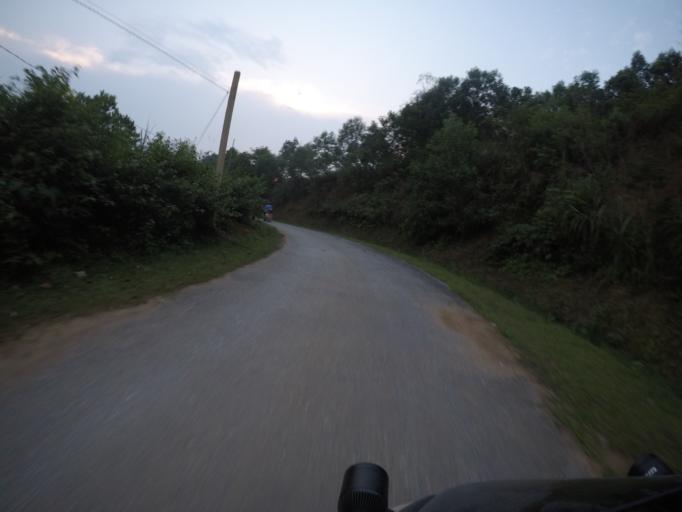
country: VN
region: Thai Nguyen
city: Chua Hang
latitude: 21.5834
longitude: 105.7079
